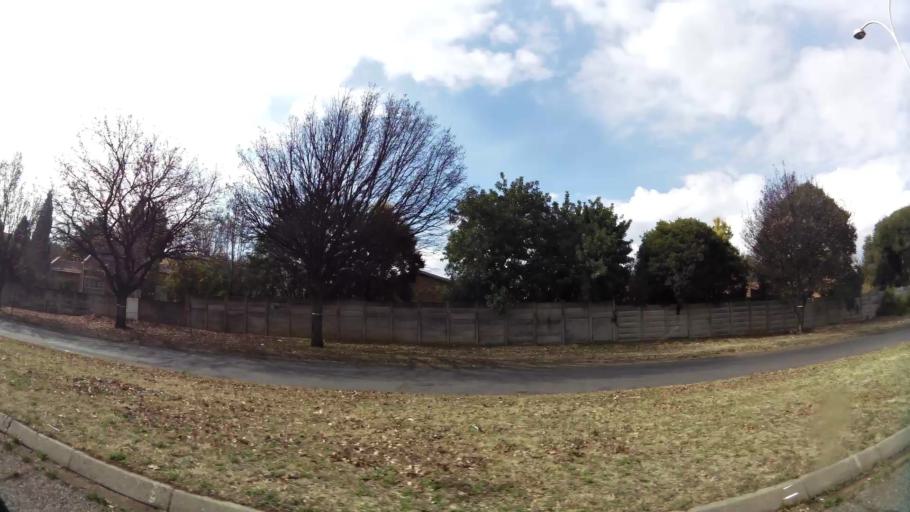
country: ZA
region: Gauteng
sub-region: Sedibeng District Municipality
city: Vanderbijlpark
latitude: -26.7364
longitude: 27.8433
